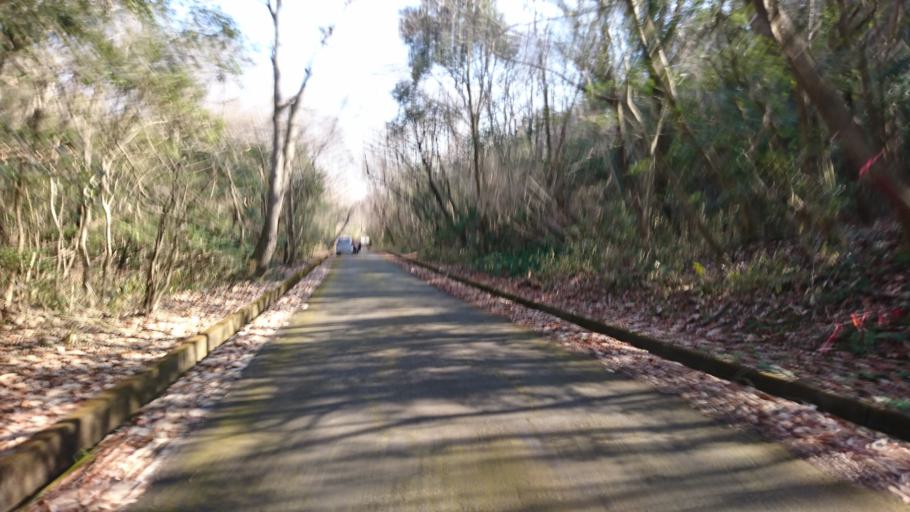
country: JP
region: Hyogo
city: Kakogawacho-honmachi
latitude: 34.8243
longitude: 134.8644
